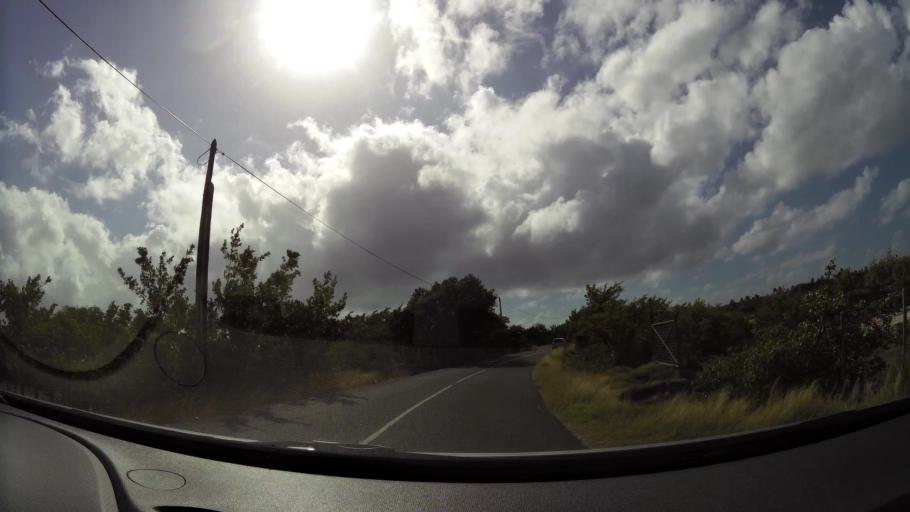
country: MQ
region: Martinique
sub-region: Martinique
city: Le Marin
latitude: 14.4066
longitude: -60.8757
